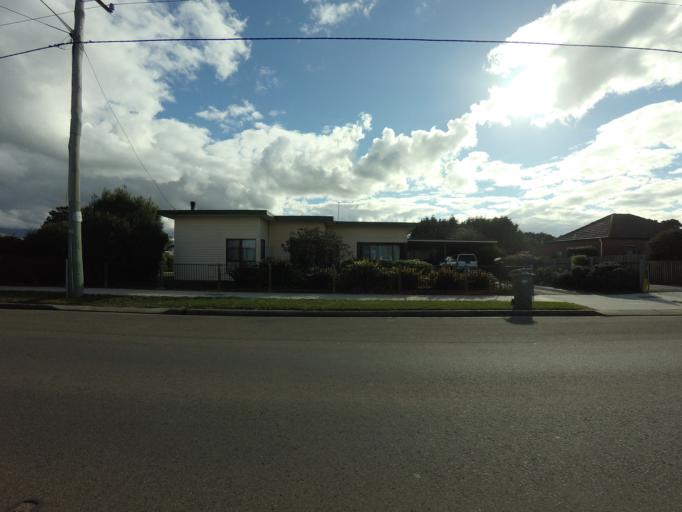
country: AU
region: Tasmania
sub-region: Northern Midlands
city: Longford
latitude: -41.6928
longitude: 147.0788
